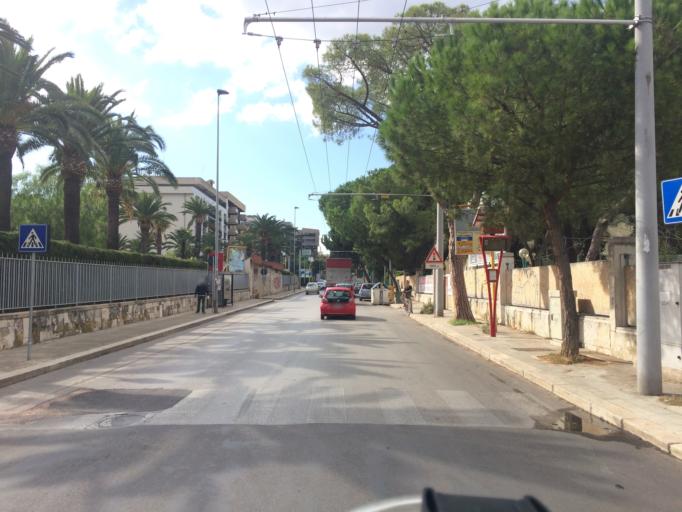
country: IT
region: Apulia
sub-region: Provincia di Bari
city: Bari
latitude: 41.0969
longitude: 16.8710
